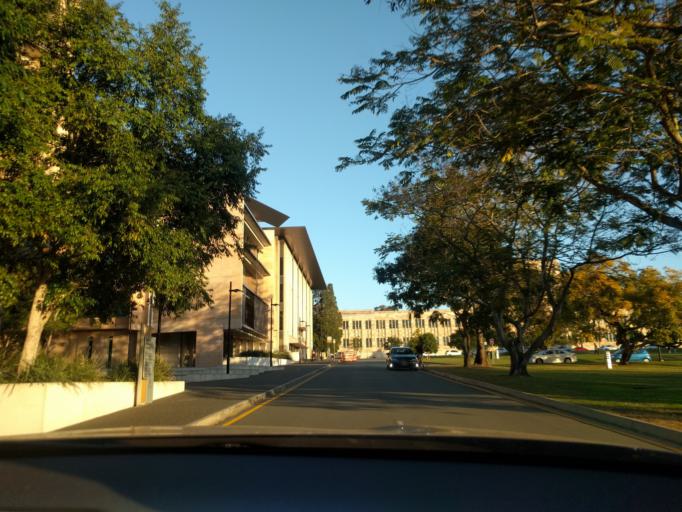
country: AU
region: Queensland
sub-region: Brisbane
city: South Brisbane
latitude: -27.4954
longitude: 153.0131
